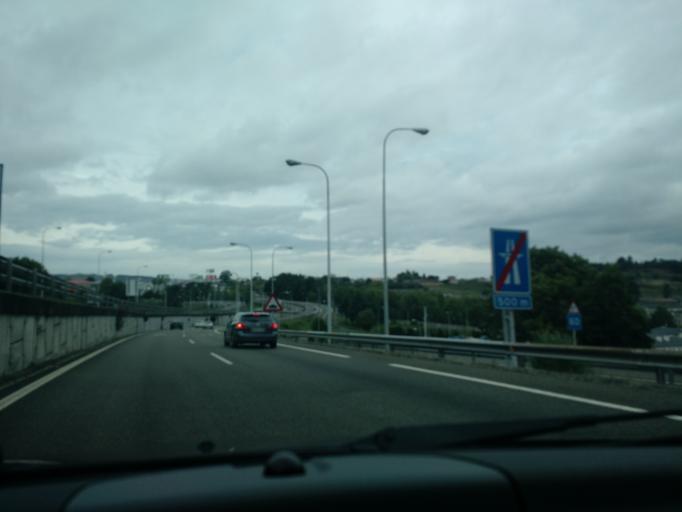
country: ES
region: Galicia
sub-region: Provincia da Coruna
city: Culleredo
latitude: 43.3271
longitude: -8.3955
